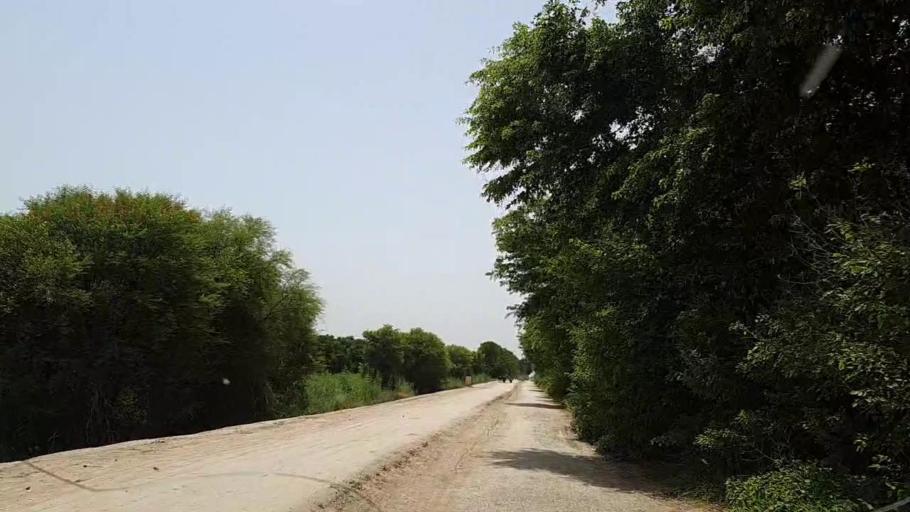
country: PK
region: Sindh
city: Tharu Shah
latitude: 26.9944
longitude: 68.1075
